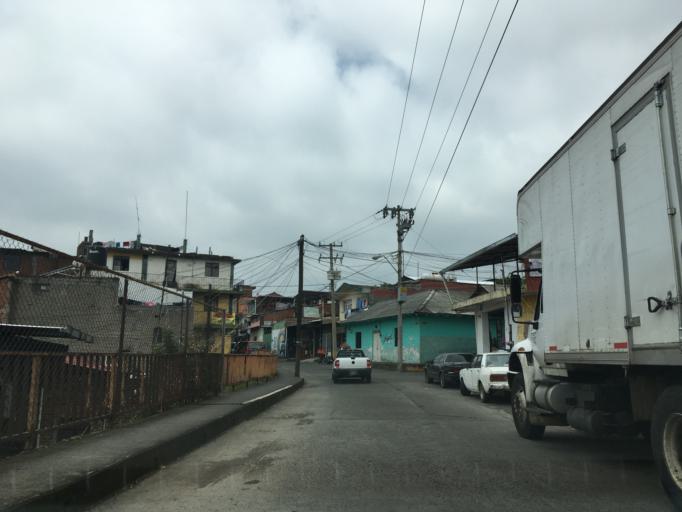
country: MX
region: Michoacan
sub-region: Uruapan
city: Uruapan
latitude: 19.4213
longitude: -102.0578
